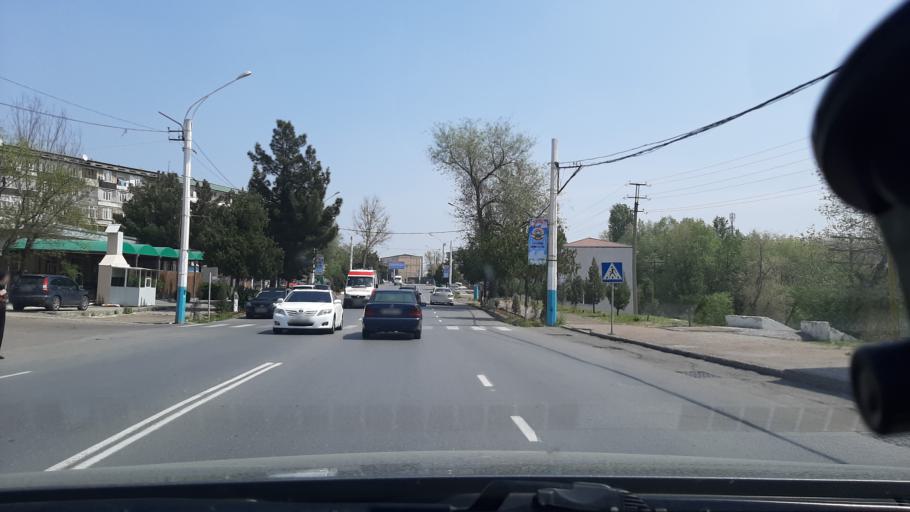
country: TJ
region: Viloyati Sughd
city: Khujand
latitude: 40.2949
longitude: 69.6038
